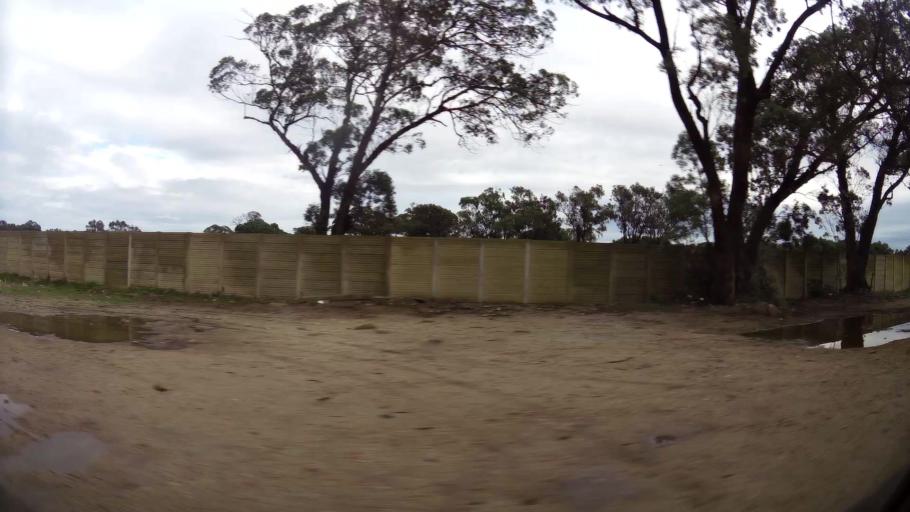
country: ZA
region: Eastern Cape
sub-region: Nelson Mandela Bay Metropolitan Municipality
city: Port Elizabeth
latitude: -33.9947
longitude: 25.5785
